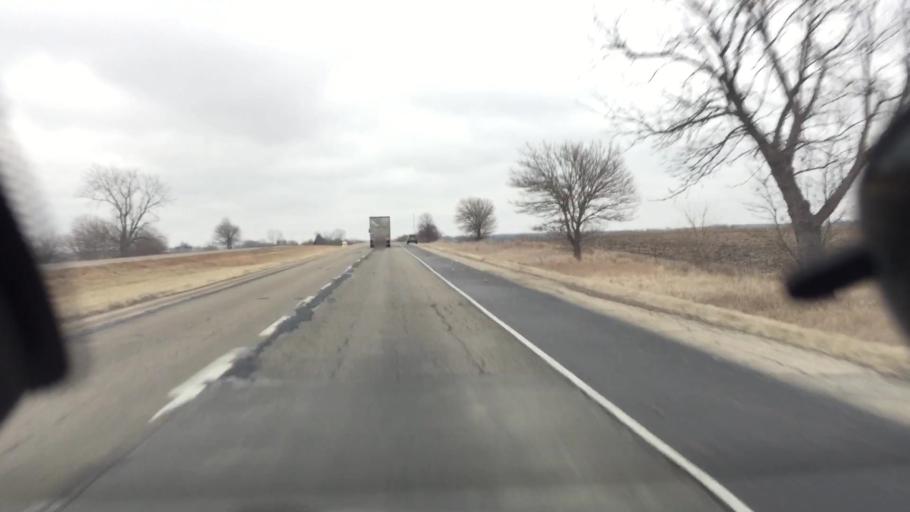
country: US
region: Illinois
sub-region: Tazewell County
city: Mackinaw
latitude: 40.6223
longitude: -89.3270
